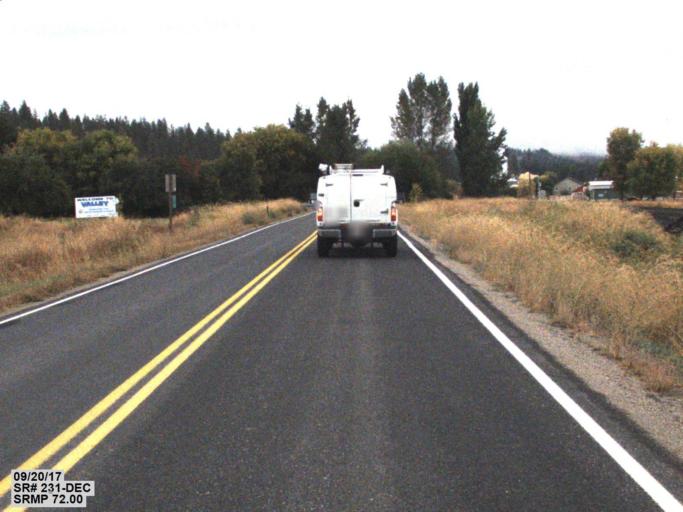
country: US
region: Washington
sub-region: Stevens County
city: Chewelah
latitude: 48.1772
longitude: -117.7275
